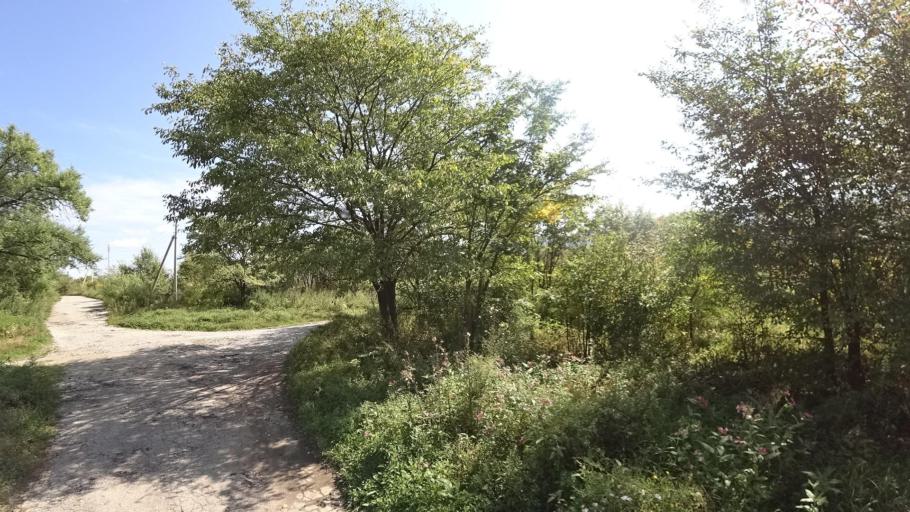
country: RU
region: Jewish Autonomous Oblast
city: Londoko
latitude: 49.0015
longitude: 131.8574
